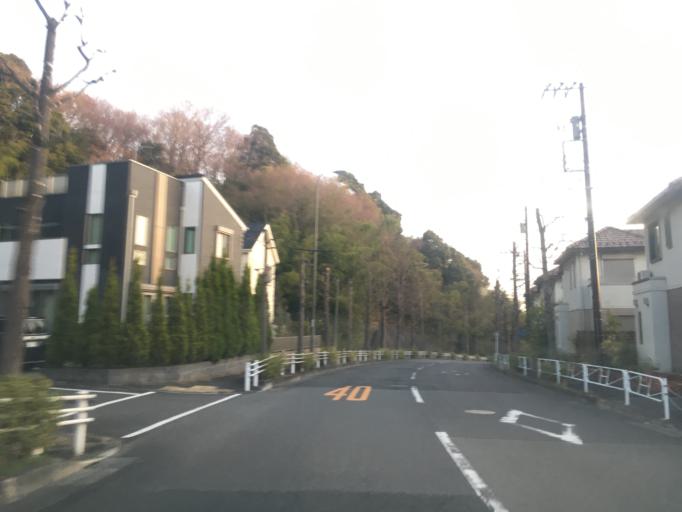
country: JP
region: Tokyo
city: Hachioji
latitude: 35.6115
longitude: 139.3572
